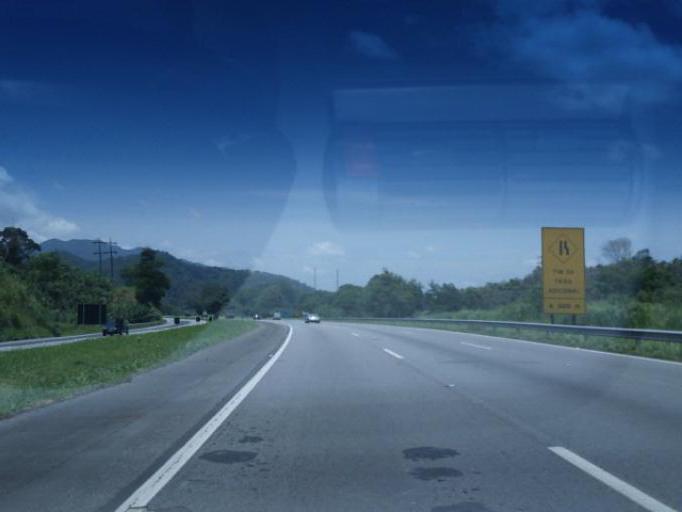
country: BR
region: Sao Paulo
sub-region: Miracatu
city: Miracatu
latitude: -24.3168
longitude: -47.5280
